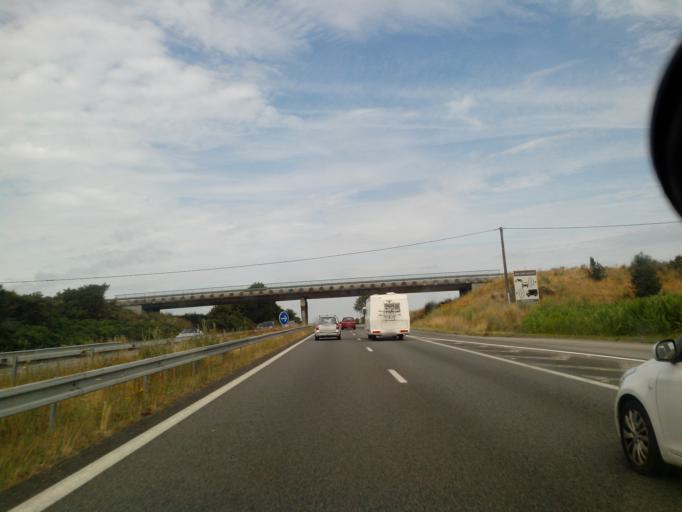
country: FR
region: Brittany
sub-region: Departement du Morbihan
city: Theix
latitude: 47.6359
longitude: -2.6660
